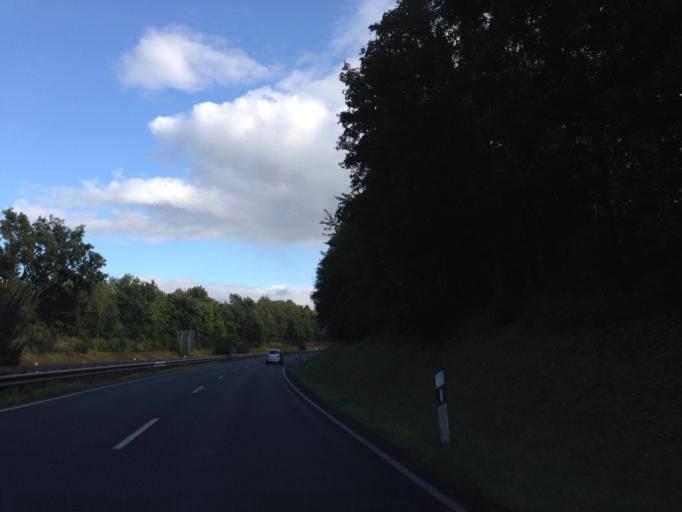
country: DE
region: Lower Saxony
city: Adendorf
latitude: 53.2675
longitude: 10.4380
